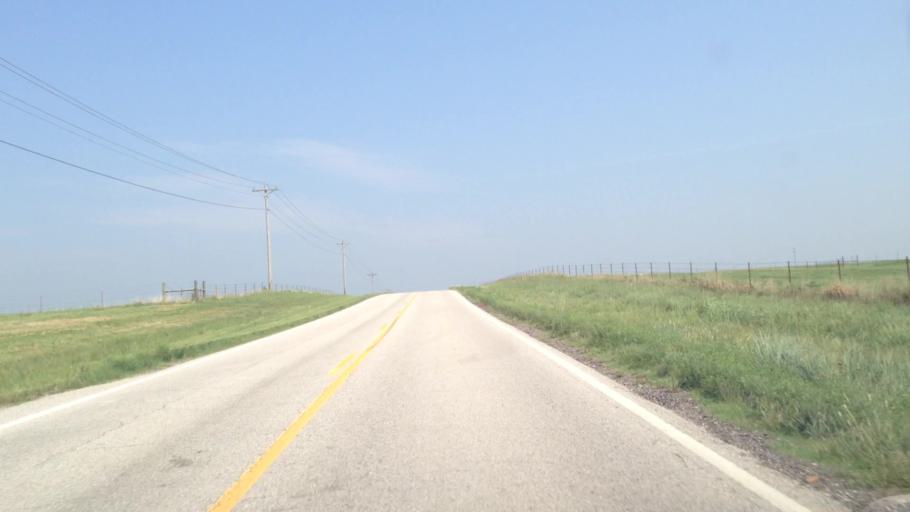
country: US
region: Oklahoma
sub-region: Craig County
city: Vinita
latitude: 36.7388
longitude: -95.1435
